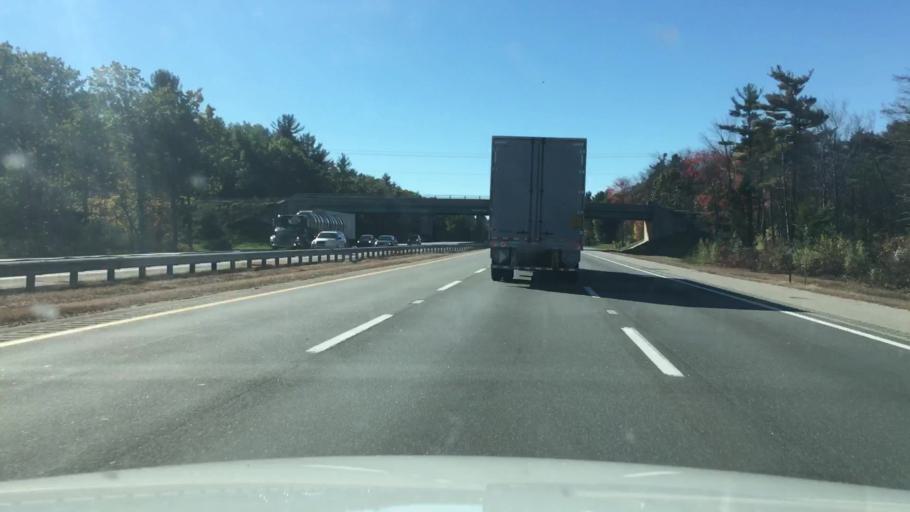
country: US
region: Maine
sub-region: York County
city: Wells Beach Station
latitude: 43.2989
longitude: -70.6159
